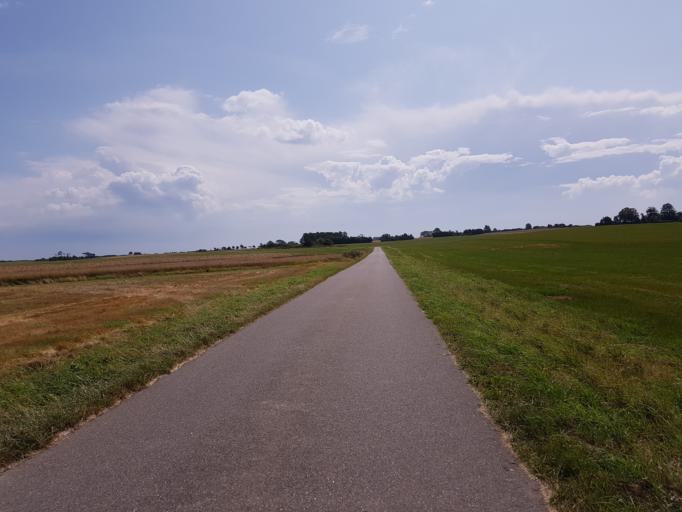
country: DK
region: Zealand
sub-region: Guldborgsund Kommune
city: Nykobing Falster
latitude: 54.5828
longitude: 11.9587
